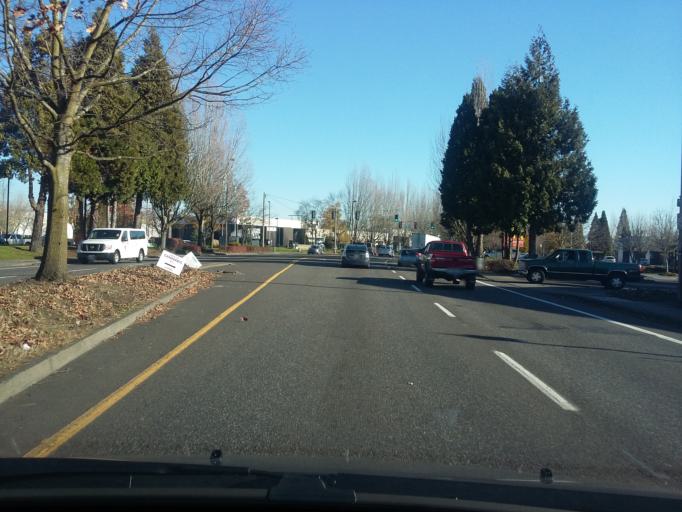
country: US
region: Washington
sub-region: Clark County
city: Mill Plain
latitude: 45.5672
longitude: -122.5392
